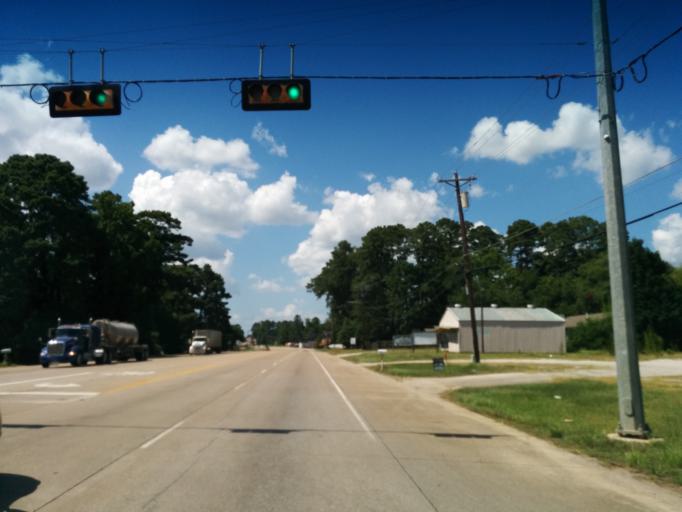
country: US
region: Texas
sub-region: Jasper County
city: Jasper
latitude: 30.9004
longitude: -93.9929
